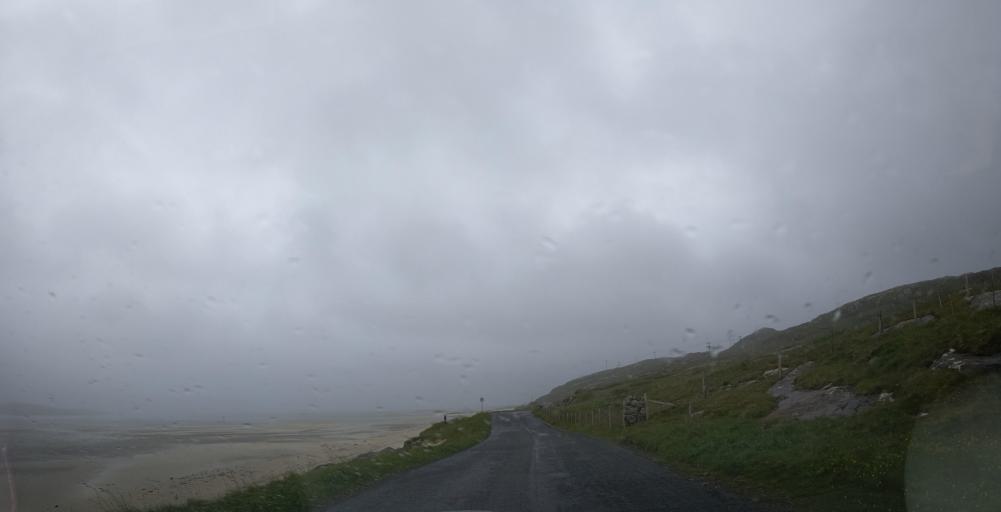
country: GB
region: Scotland
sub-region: Eilean Siar
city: Barra
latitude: 57.0190
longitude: -7.4430
